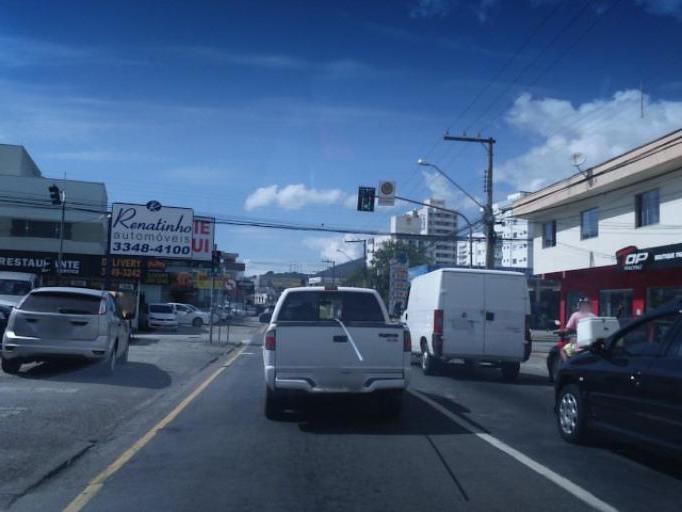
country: BR
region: Santa Catarina
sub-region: Itajai
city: Itajai
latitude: -26.8978
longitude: -48.6743
